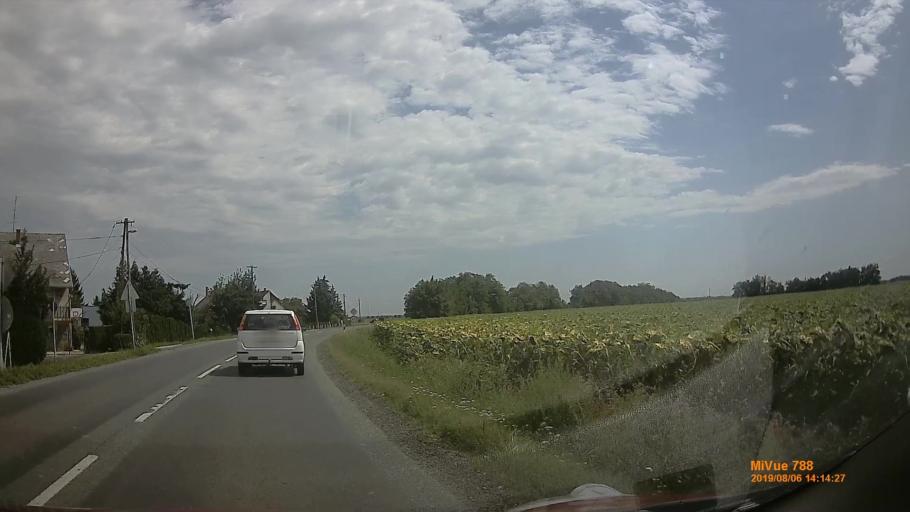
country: HU
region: Vas
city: Taplanszentkereszt
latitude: 47.1967
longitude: 16.6896
